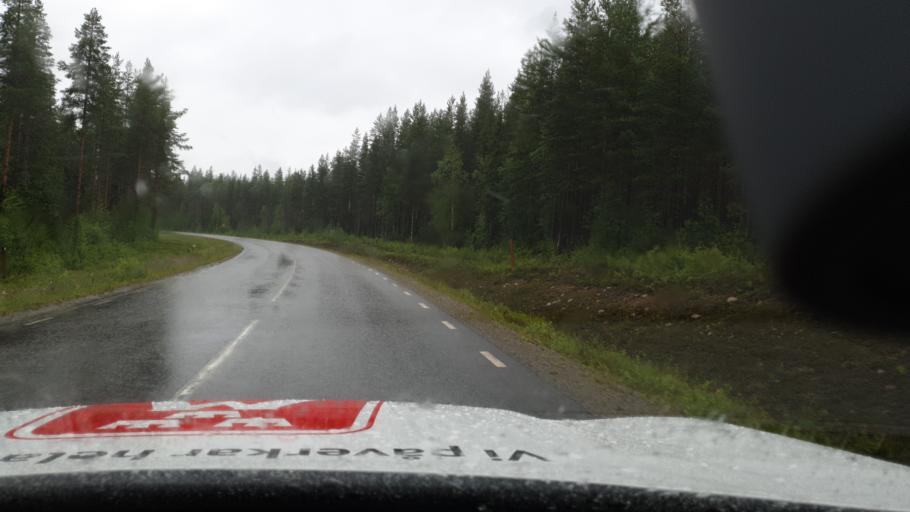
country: SE
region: Vaesterbotten
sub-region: Skelleftea Kommun
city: Langsele
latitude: 64.8353
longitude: 19.9036
